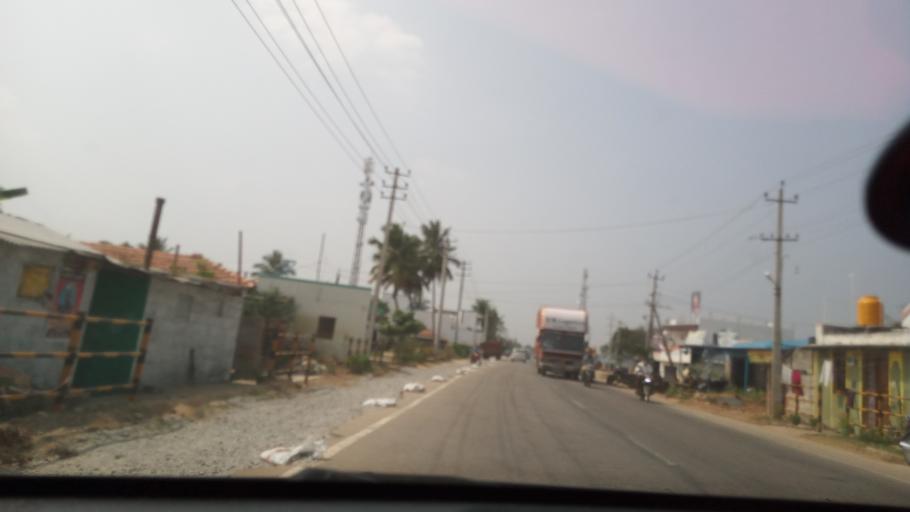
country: IN
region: Karnataka
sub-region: Chamrajnagar
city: Chamrajnagar
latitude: 11.9892
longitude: 76.8694
